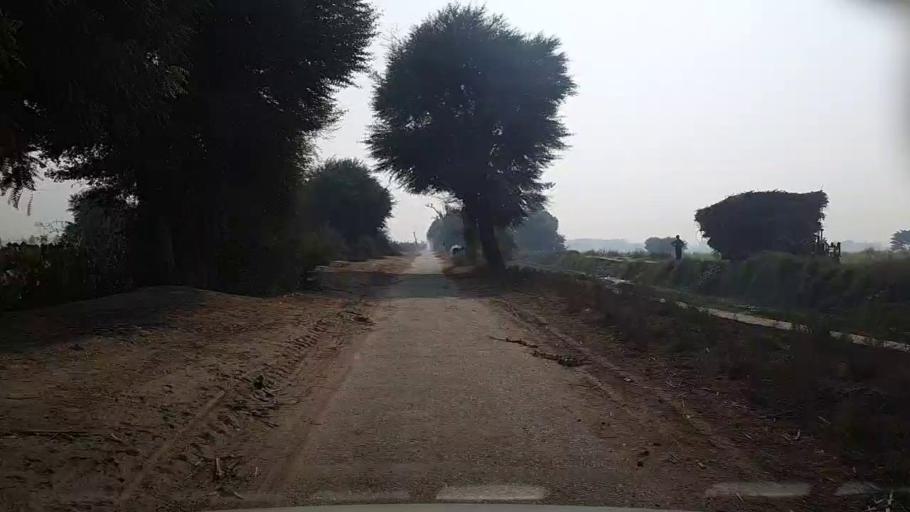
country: PK
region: Sindh
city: Setharja Old
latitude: 27.1105
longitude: 68.5088
